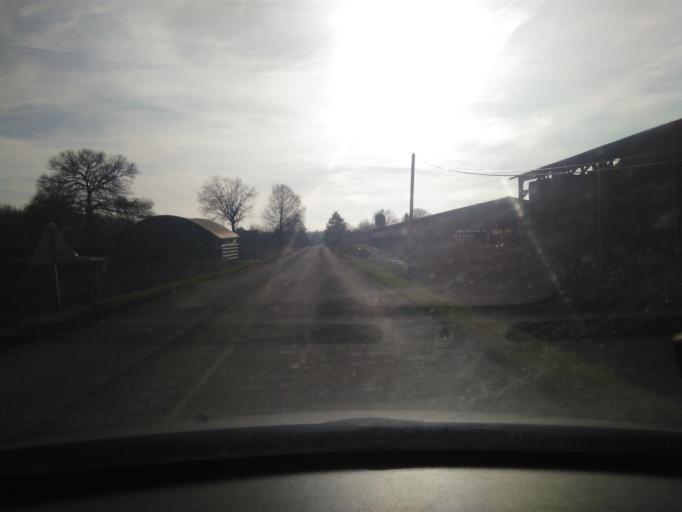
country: FR
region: Bourgogne
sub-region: Departement de la Nievre
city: Saint-Parize-le-Chatel
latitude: 46.8288
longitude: 3.2469
